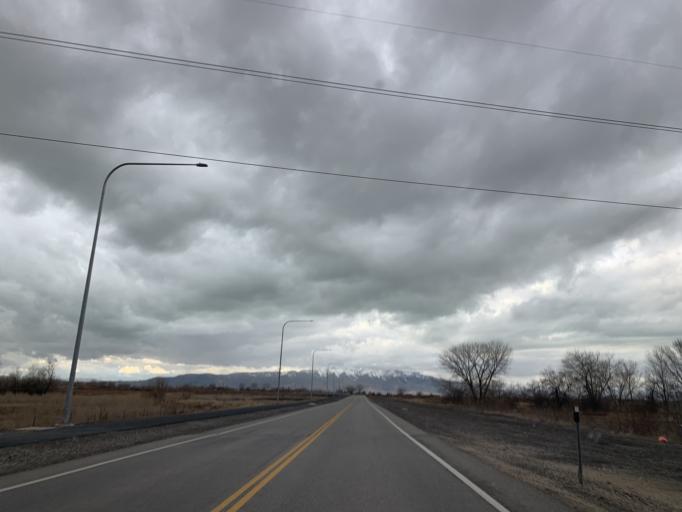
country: US
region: Utah
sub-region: Utah County
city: Provo
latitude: 40.2173
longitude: -111.6948
